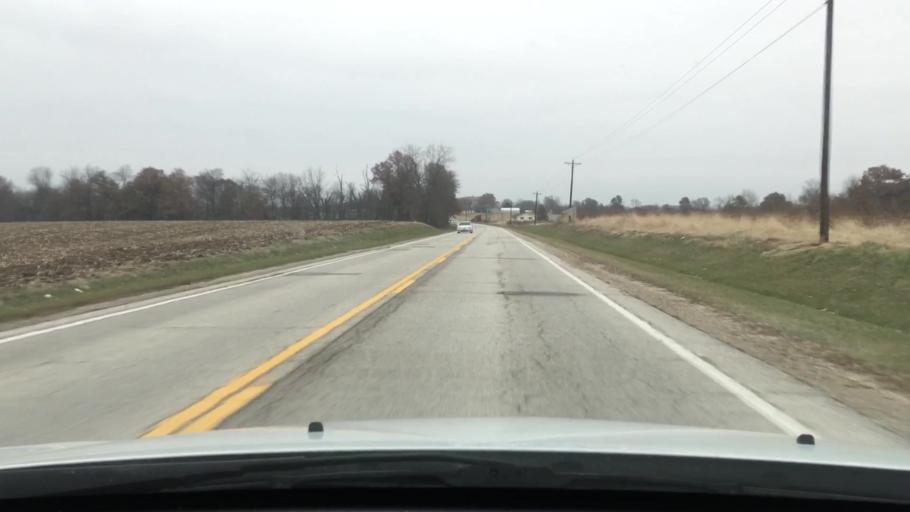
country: US
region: Illinois
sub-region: Pike County
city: Pittsfield
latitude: 39.5661
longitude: -90.9154
